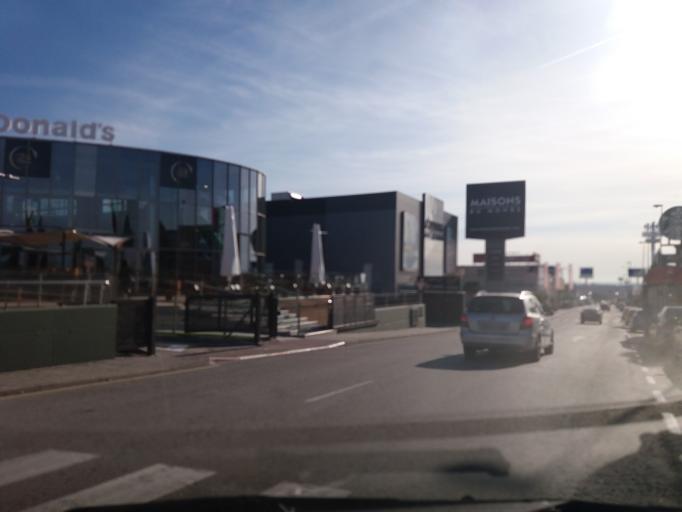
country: ES
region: Madrid
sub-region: Provincia de Madrid
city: Majadahonda
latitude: 40.4559
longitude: -3.8738
